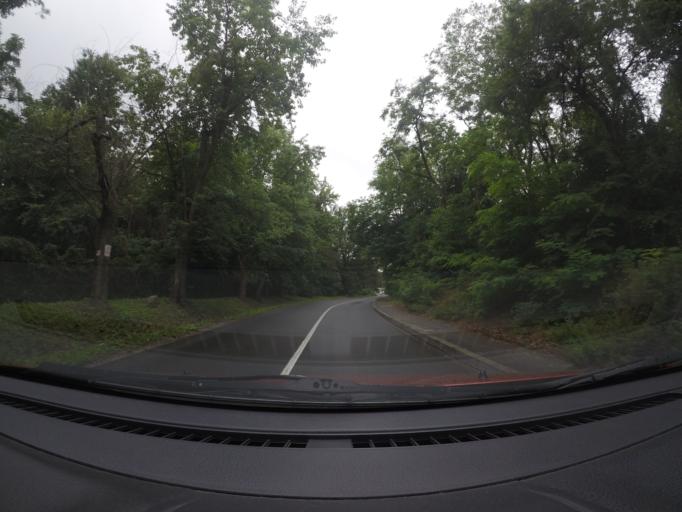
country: RS
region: Central Serbia
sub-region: Belgrade
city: Zvezdara
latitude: 44.6850
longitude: 20.5469
